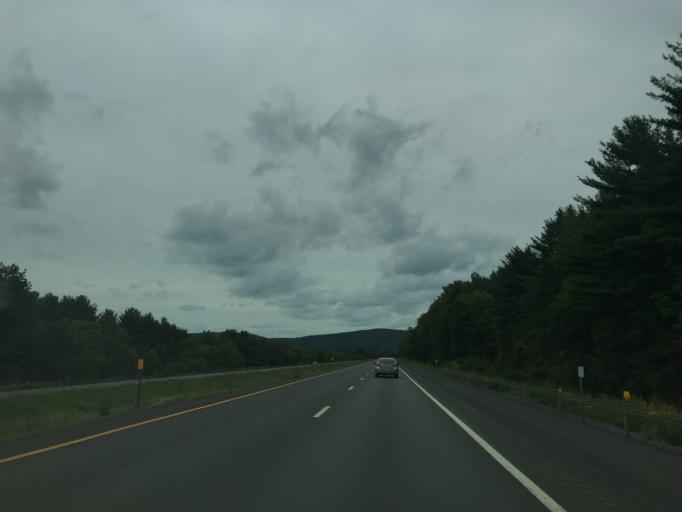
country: US
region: New York
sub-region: Delaware County
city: Sidney
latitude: 42.2993
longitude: -75.3817
